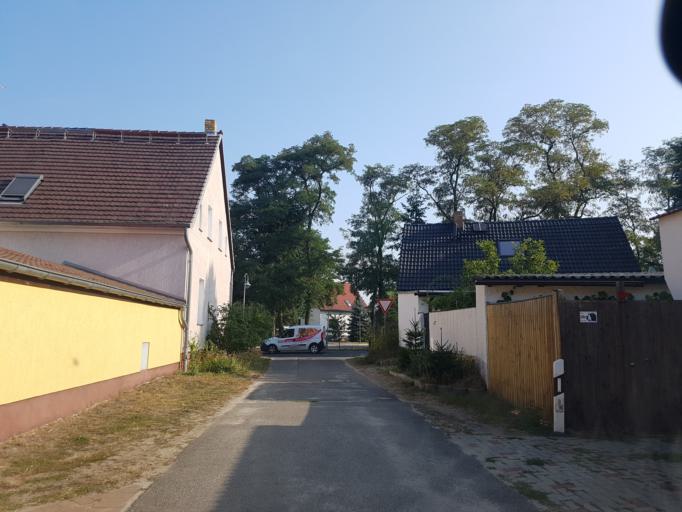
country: DE
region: Brandenburg
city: Finsterwalde
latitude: 51.6401
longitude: 13.7379
